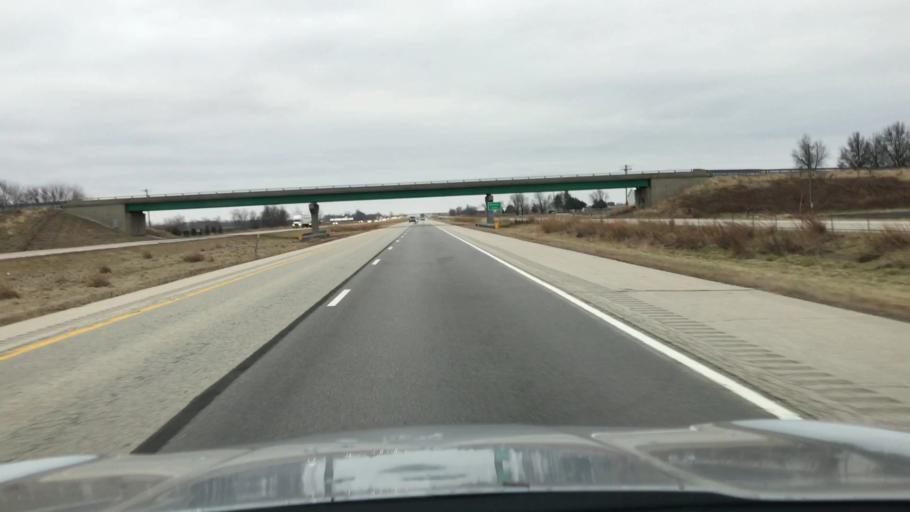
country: US
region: Illinois
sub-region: Sangamon County
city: Divernon
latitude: 39.5252
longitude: -89.6459
